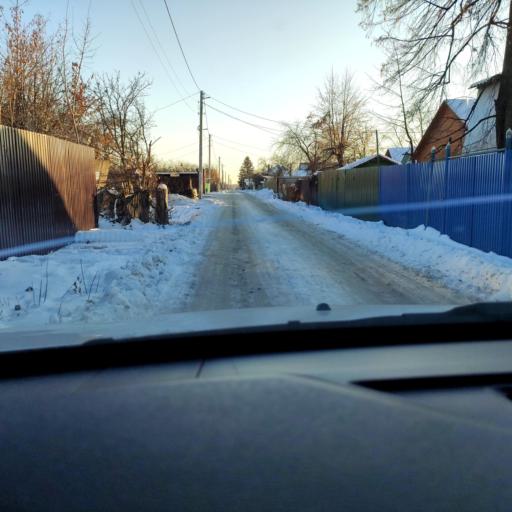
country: RU
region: Samara
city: Petra-Dubrava
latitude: 53.2868
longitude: 50.2911
